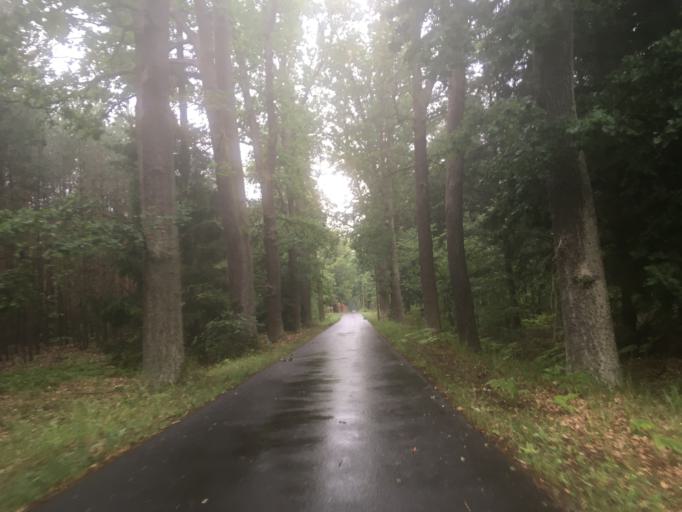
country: DE
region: Brandenburg
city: Liebenwalde
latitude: 52.8521
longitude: 13.4391
